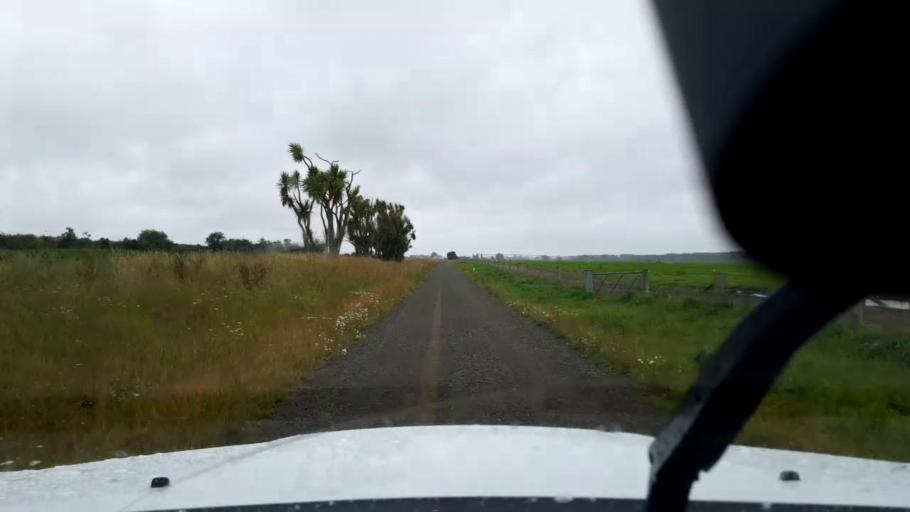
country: NZ
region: Canterbury
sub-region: Timaru District
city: Pleasant Point
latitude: -44.2542
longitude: 171.1872
